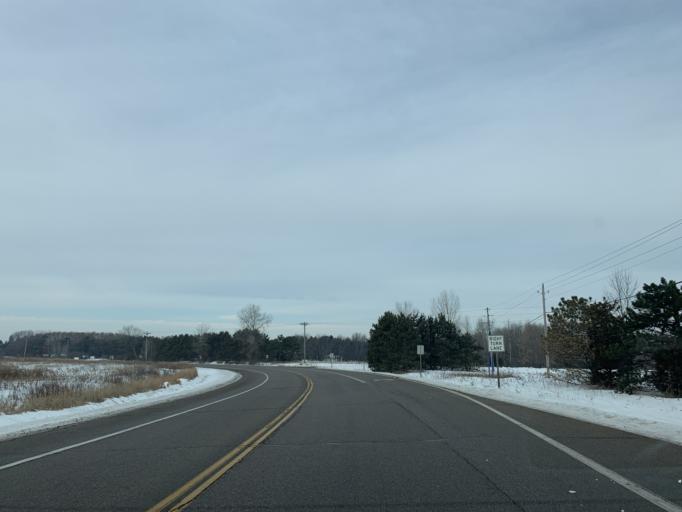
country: US
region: Minnesota
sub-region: Washington County
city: Forest Lake
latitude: 45.2856
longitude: -93.0152
